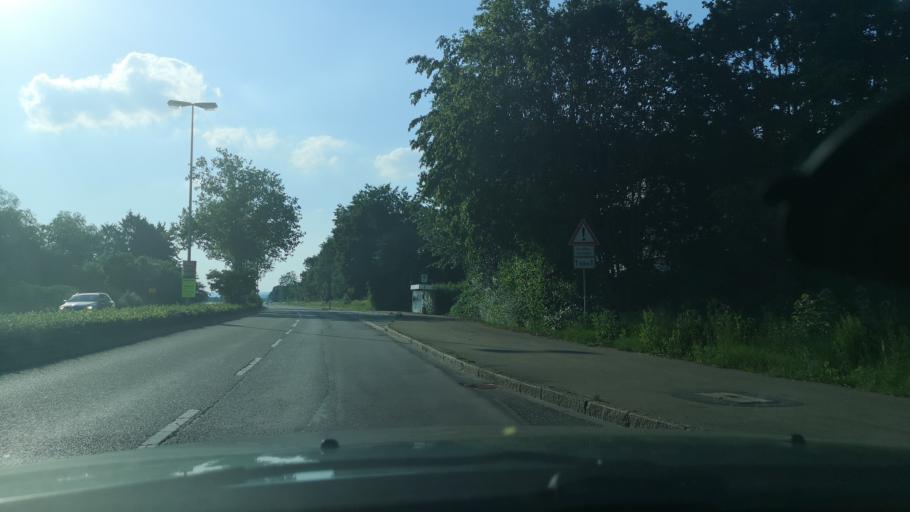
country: DE
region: Baden-Wuerttemberg
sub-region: Regierungsbezirk Stuttgart
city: Sussen
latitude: 48.6798
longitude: 9.7485
